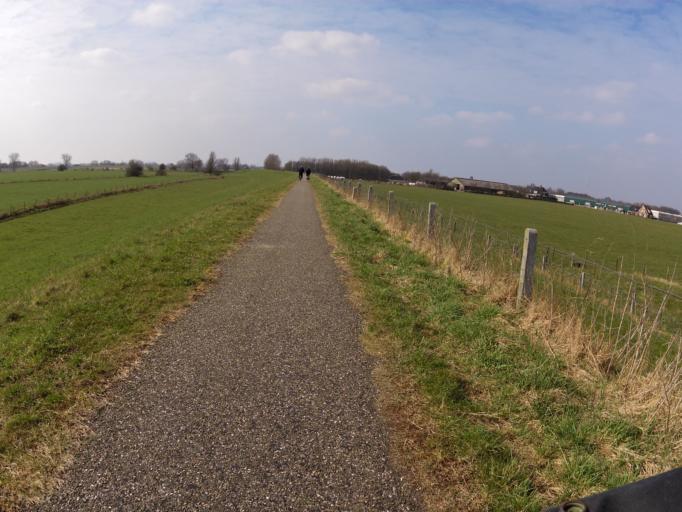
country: NL
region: Gelderland
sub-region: Gemeente Maasdriel
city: Hedel
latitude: 51.7427
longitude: 5.2444
